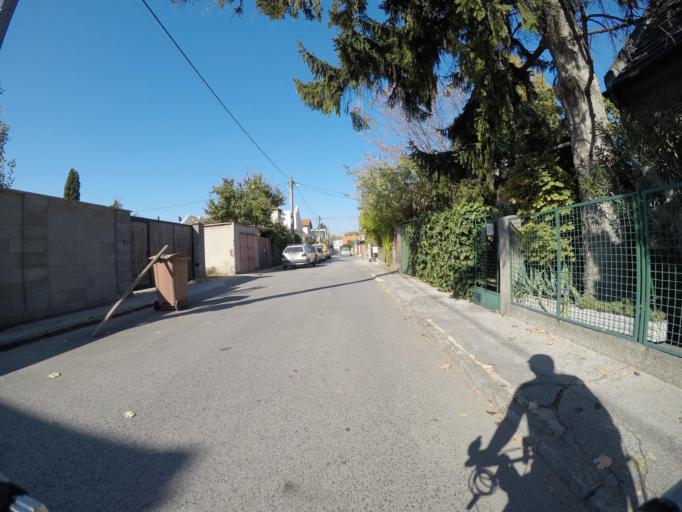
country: SK
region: Bratislavsky
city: Bratislava
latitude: 48.1715
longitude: 17.1640
